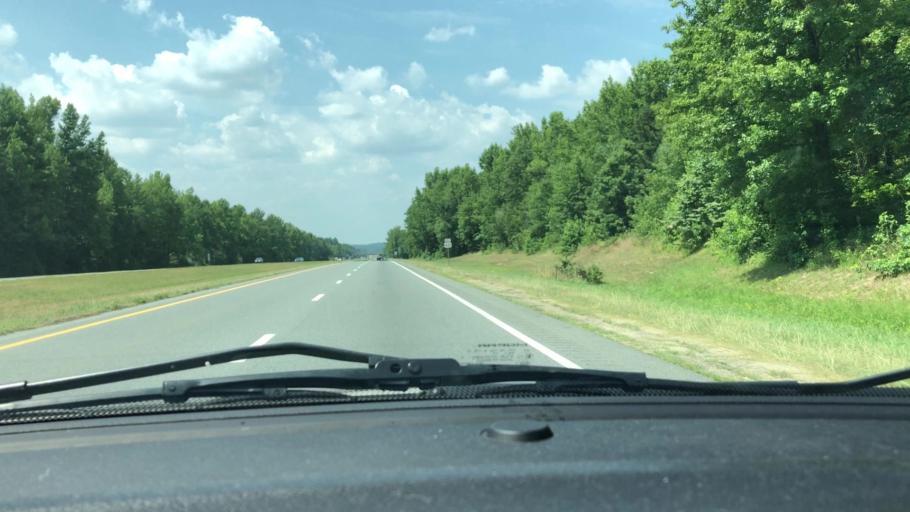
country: US
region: North Carolina
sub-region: Guilford County
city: Forest Oaks
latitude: 35.9227
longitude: -79.6784
